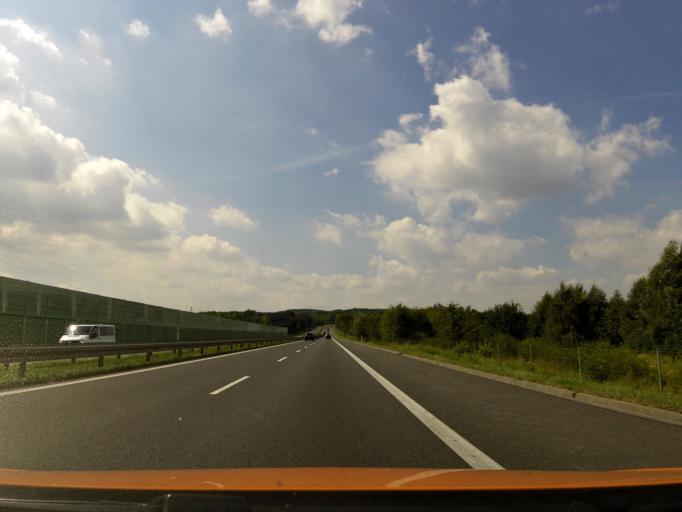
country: PL
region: West Pomeranian Voivodeship
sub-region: Powiat gryfinski
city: Stare Czarnowo
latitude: 53.3645
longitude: 14.6804
